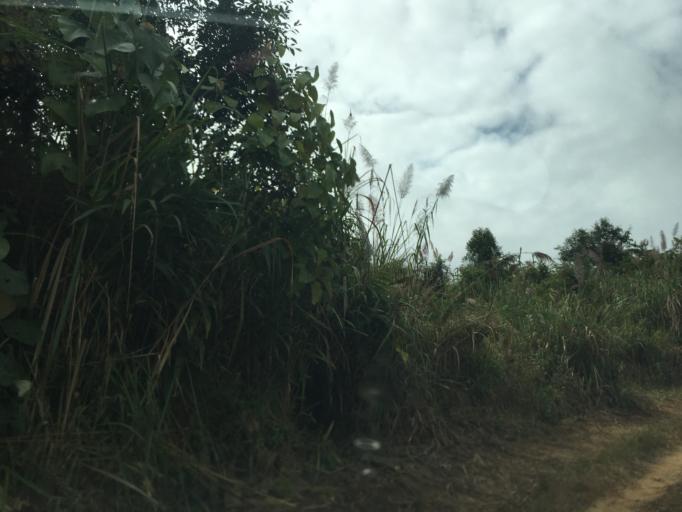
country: LA
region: Houaphan
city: Viengthong
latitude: 19.9297
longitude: 103.2965
